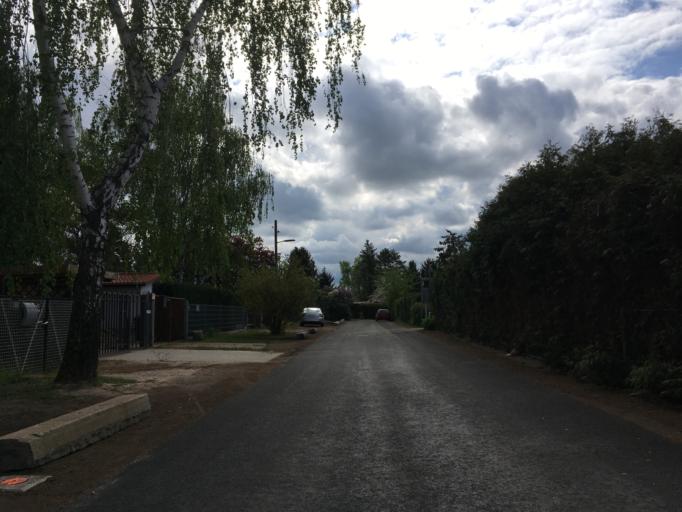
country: DE
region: Berlin
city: Buchholz
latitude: 52.6089
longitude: 13.4434
